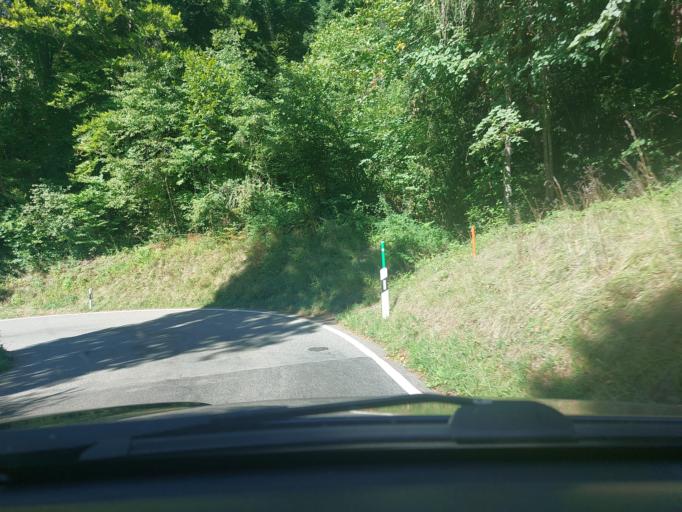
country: CH
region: Vaud
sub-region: Aigle District
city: Aigle
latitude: 46.3391
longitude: 6.9663
